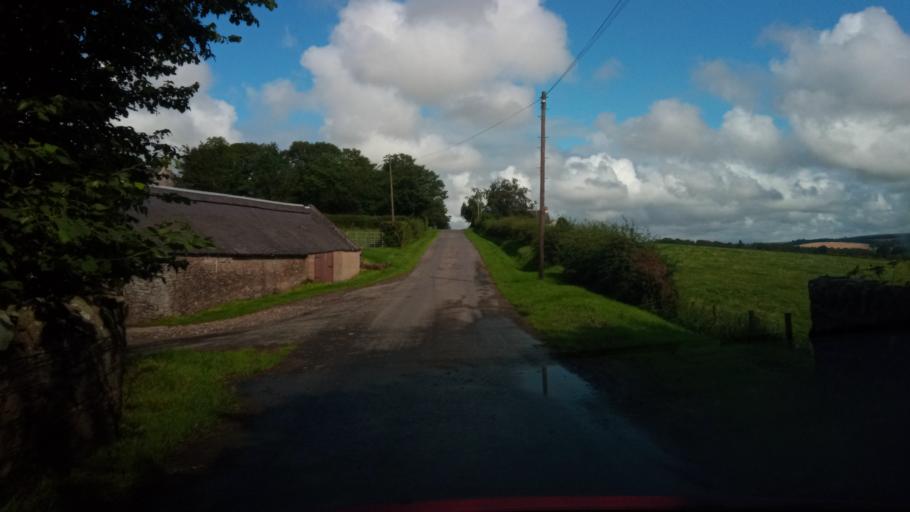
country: GB
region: Scotland
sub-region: The Scottish Borders
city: Earlston
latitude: 55.6555
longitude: -2.7092
